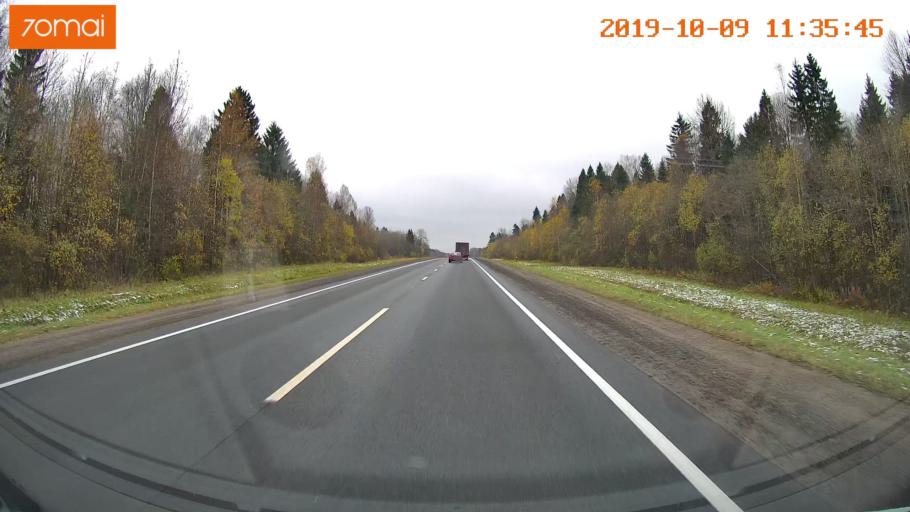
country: RU
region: Vologda
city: Gryazovets
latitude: 58.9993
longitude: 40.1294
